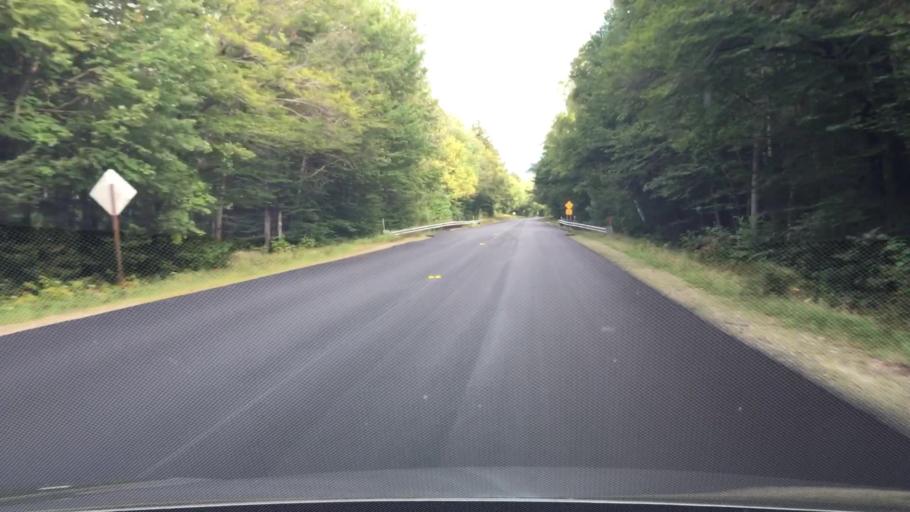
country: US
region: New Hampshire
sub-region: Carroll County
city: Sandwich
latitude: 44.0051
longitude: -71.4223
